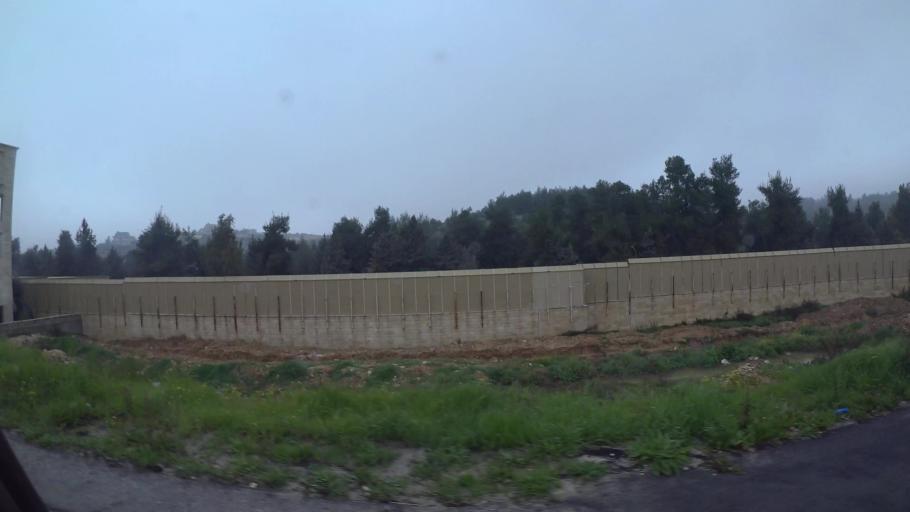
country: JO
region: Amman
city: Wadi as Sir
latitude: 32.0013
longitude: 35.8182
